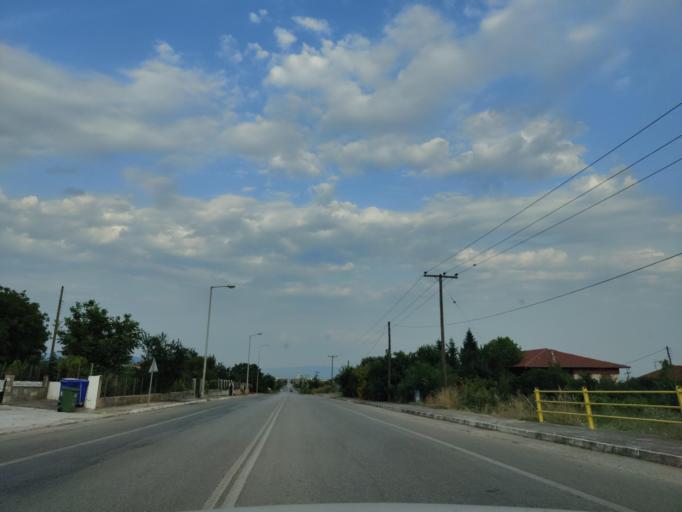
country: GR
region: East Macedonia and Thrace
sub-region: Nomos Dramas
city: Petroussa
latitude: 41.1686
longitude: 24.0459
